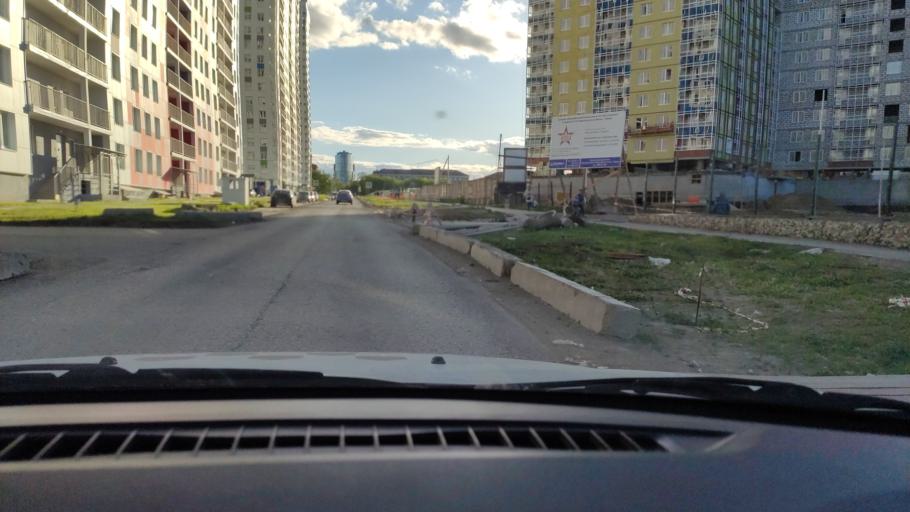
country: RU
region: Perm
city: Perm
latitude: 57.9915
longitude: 56.2645
